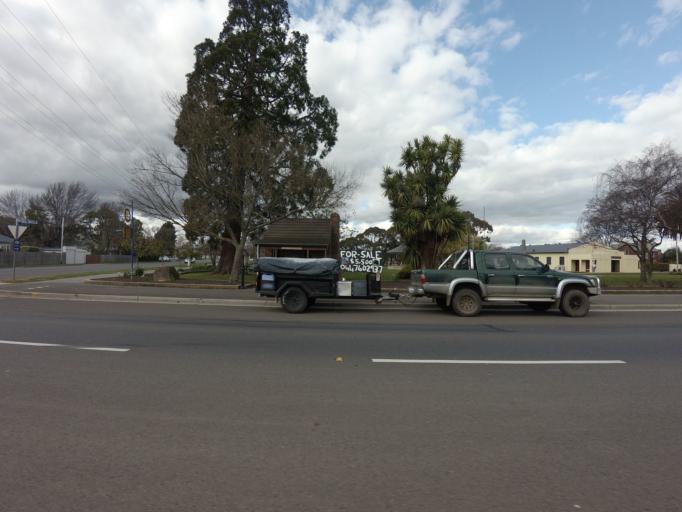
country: AU
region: Tasmania
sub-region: Northern Midlands
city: Longford
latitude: -41.5928
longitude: 147.1216
